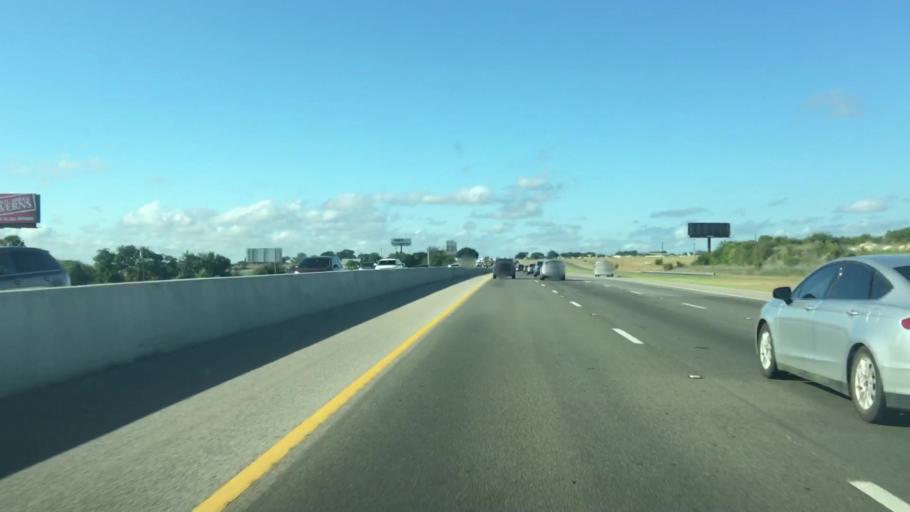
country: US
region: Texas
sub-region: Williamson County
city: Serenada
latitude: 30.7992
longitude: -97.6176
